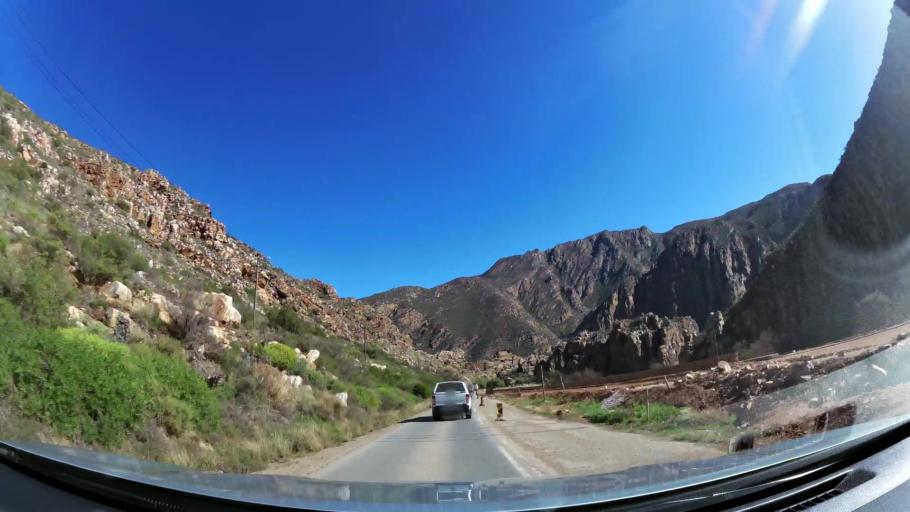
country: ZA
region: Western Cape
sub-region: Cape Winelands District Municipality
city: Ashton
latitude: -33.8031
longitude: 20.0983
